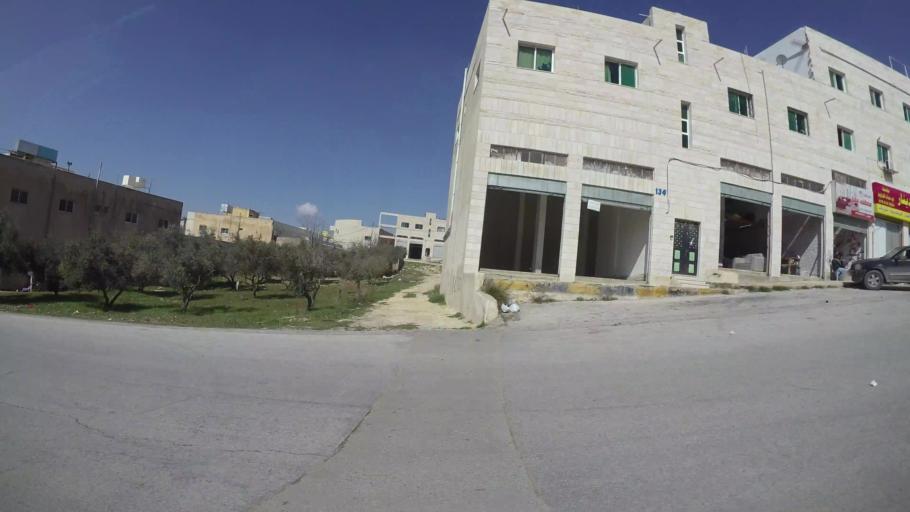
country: JO
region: Amman
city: Al Bunayyat ash Shamaliyah
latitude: 31.9036
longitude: 35.9023
